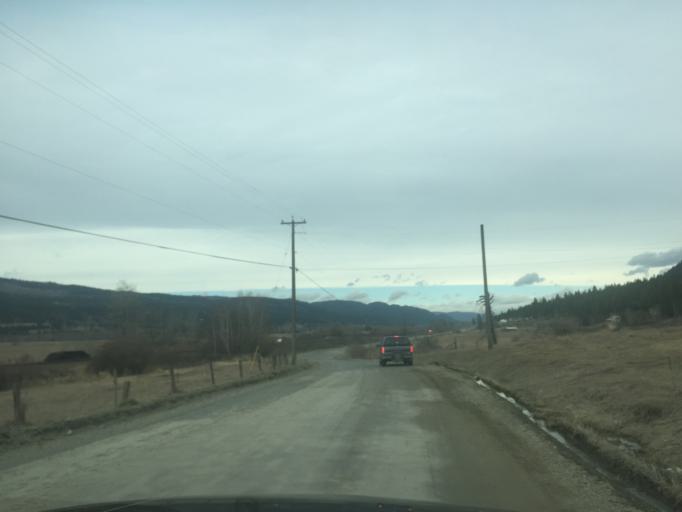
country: CA
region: British Columbia
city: Kamloops
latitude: 51.2481
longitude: -120.1489
